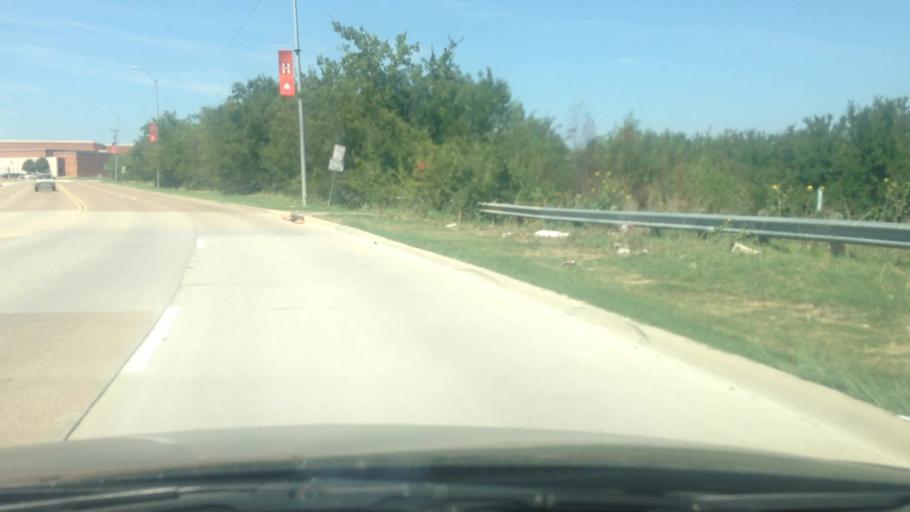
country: US
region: Texas
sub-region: Tarrant County
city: Watauga
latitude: 32.8452
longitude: -97.2758
